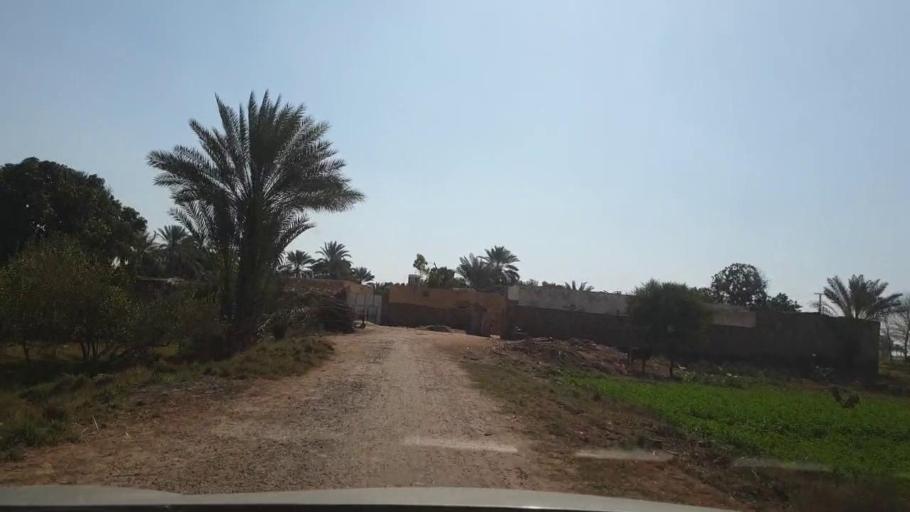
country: PK
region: Sindh
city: Tando Adam
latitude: 25.6352
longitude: 68.6854
